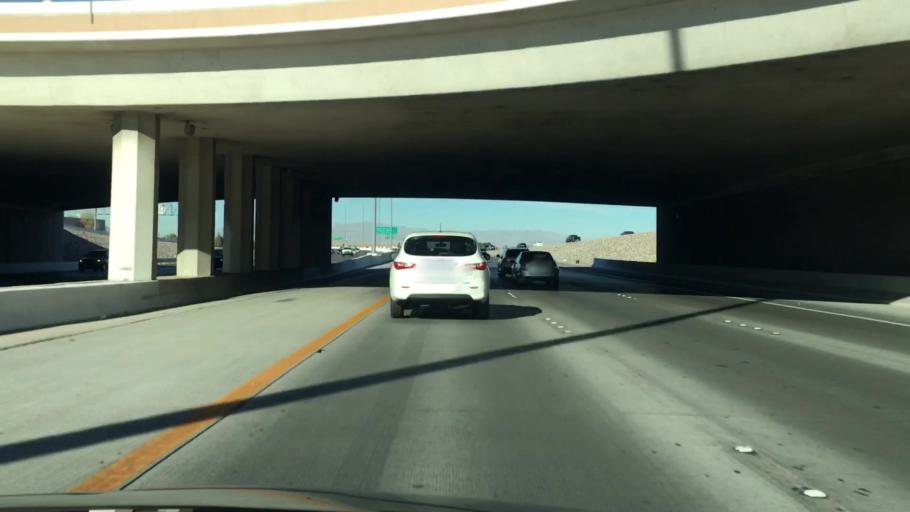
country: US
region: Nevada
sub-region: Clark County
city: Paradise
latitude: 36.0424
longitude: -115.1339
